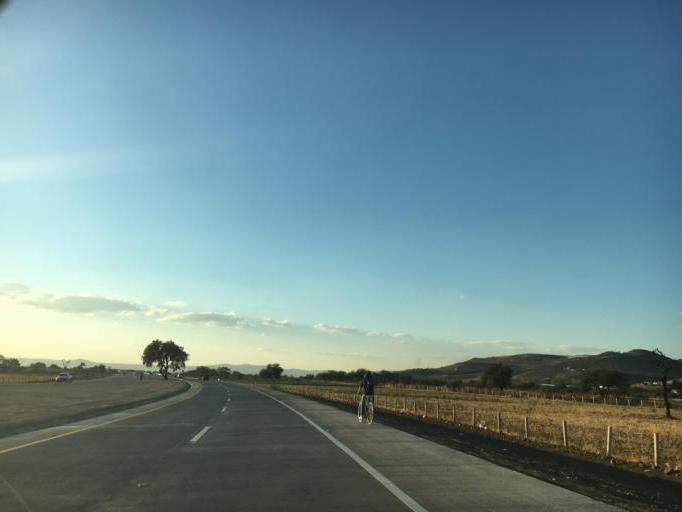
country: MX
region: Guanajuato
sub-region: Leon
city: Ladrilleras del Refugio
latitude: 21.0944
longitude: -101.5639
